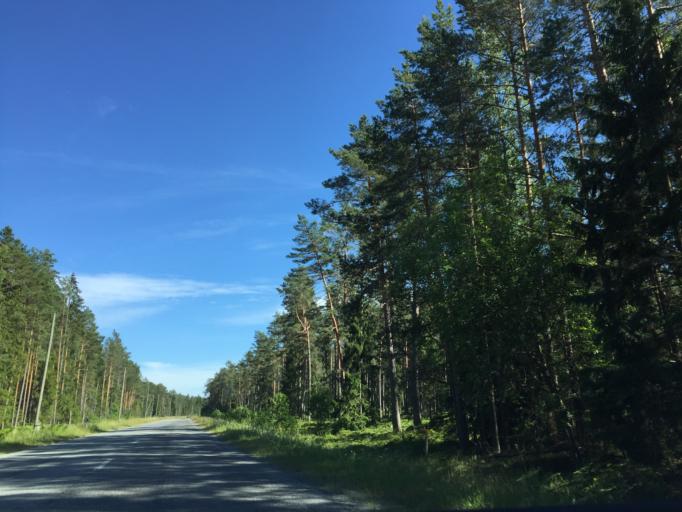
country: LV
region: Rojas
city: Roja
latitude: 57.4911
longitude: 22.8346
